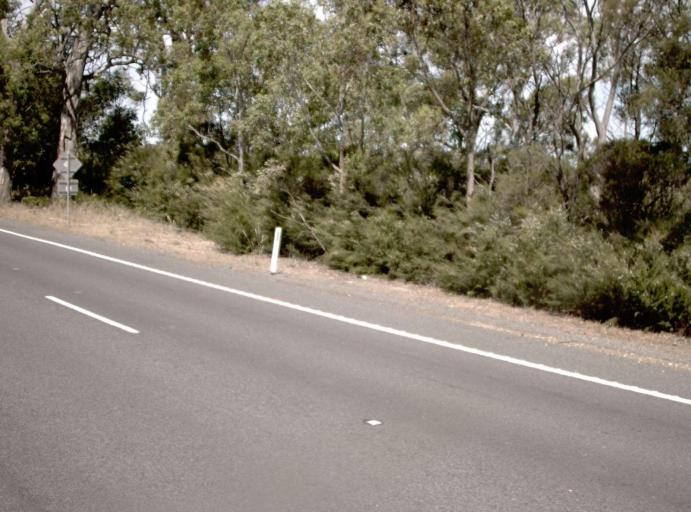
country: AU
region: Victoria
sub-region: Wellington
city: Sale
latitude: -37.9395
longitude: 147.1491
